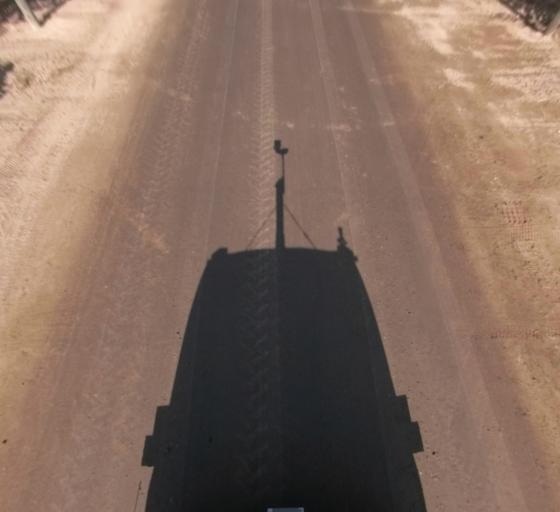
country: US
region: California
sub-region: Madera County
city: Madera Acres
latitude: 37.0328
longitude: -120.1248
